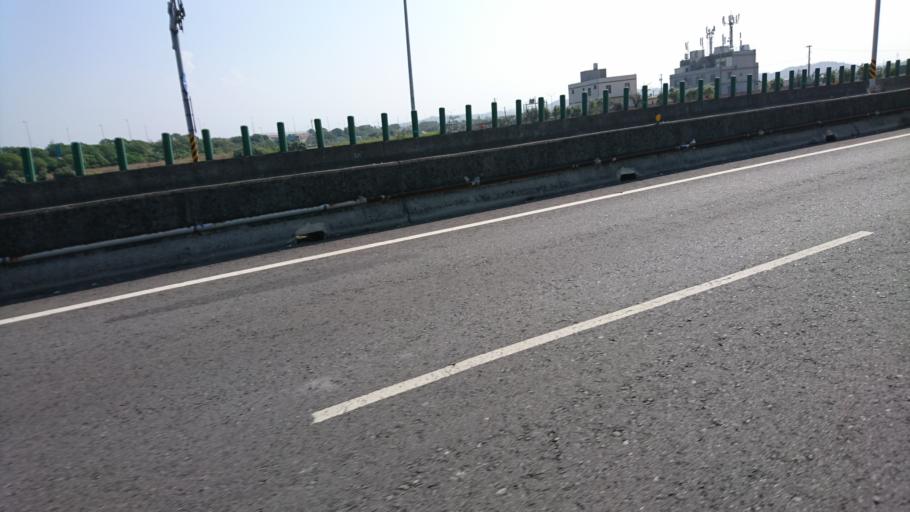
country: TW
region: Taiwan
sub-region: Miaoli
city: Miaoli
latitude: 24.6790
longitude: 120.8448
